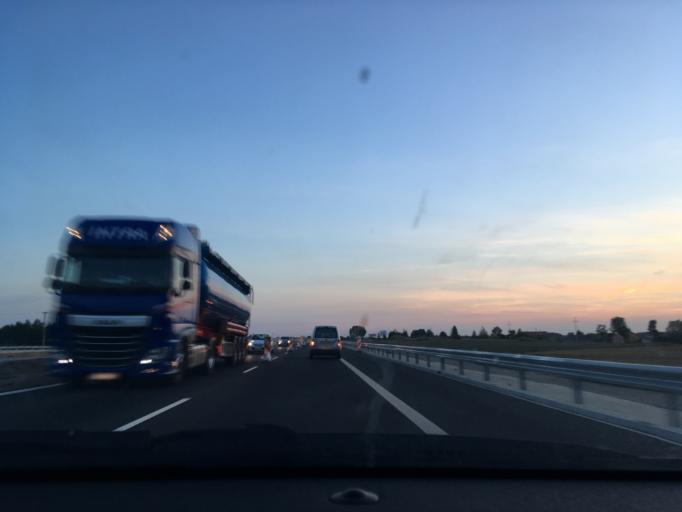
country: PL
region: Podlasie
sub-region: Powiat zambrowski
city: Zambrow
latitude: 52.9603
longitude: 22.1937
